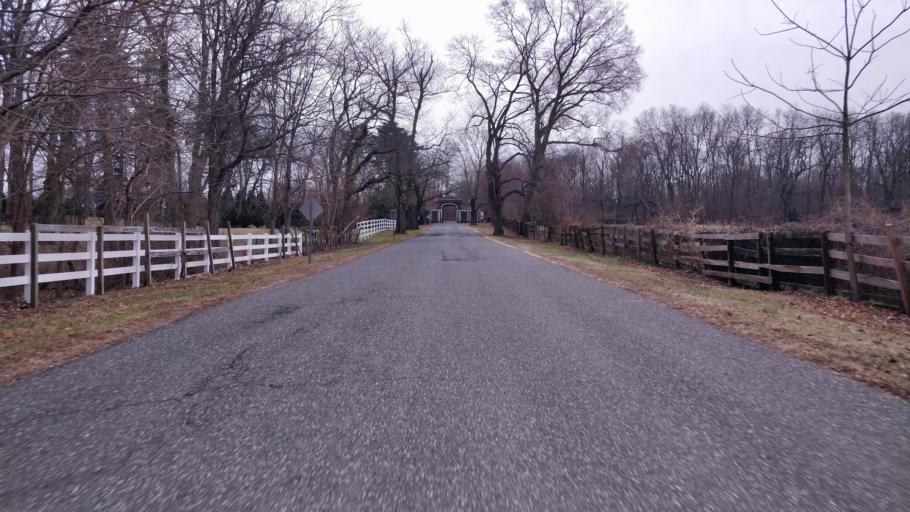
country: US
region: New York
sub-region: Nassau County
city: Old Westbury
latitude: 40.7820
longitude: -73.5786
